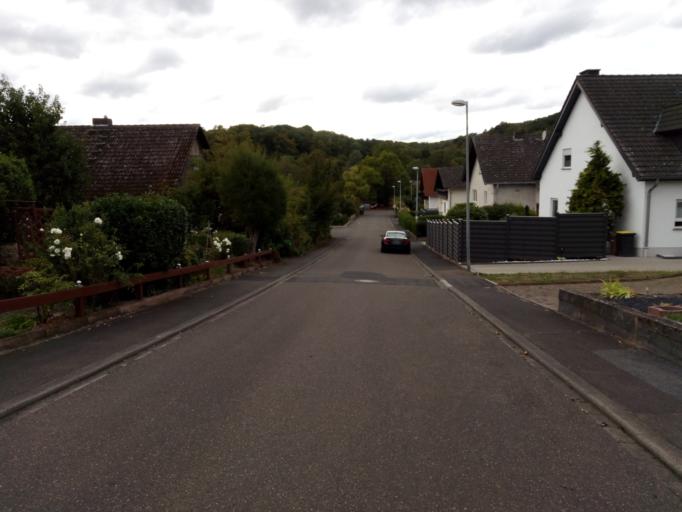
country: DE
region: Rheinland-Pfalz
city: Schweppenhausen
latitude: 49.9237
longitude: 7.8028
